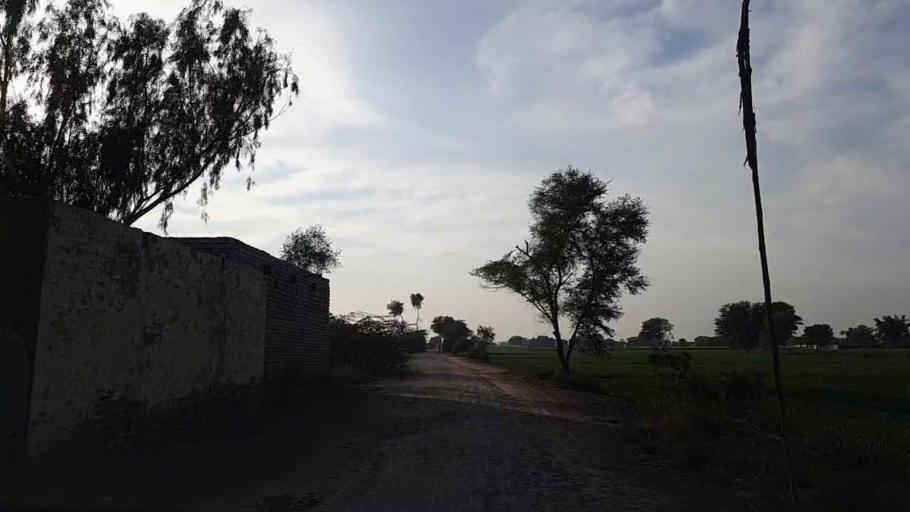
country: PK
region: Sindh
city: Bandhi
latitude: 26.5645
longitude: 68.2714
